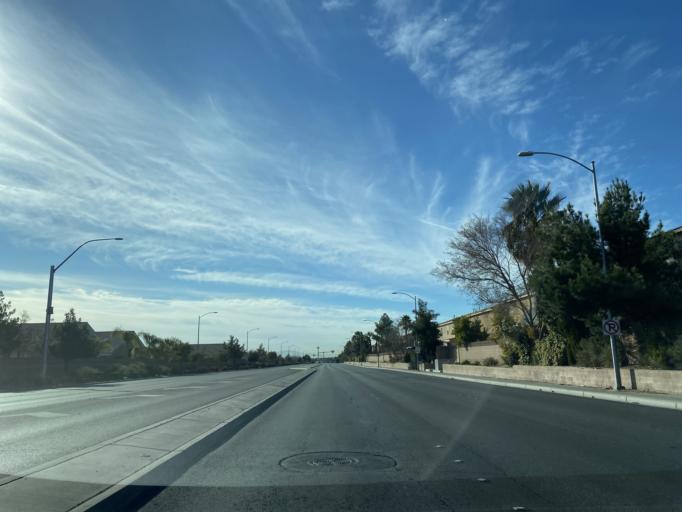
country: US
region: Nevada
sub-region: Clark County
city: North Las Vegas
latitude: 36.2686
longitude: -115.2070
